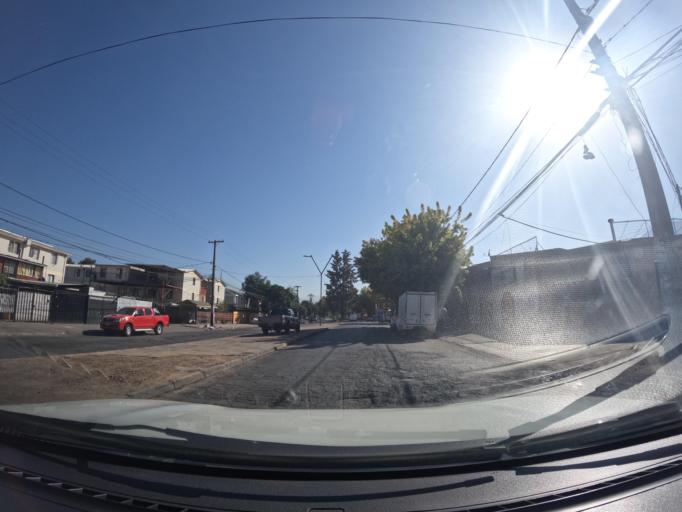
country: CL
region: Santiago Metropolitan
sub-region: Provincia de Santiago
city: Villa Presidente Frei, Nunoa, Santiago, Chile
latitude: -33.4817
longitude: -70.5670
